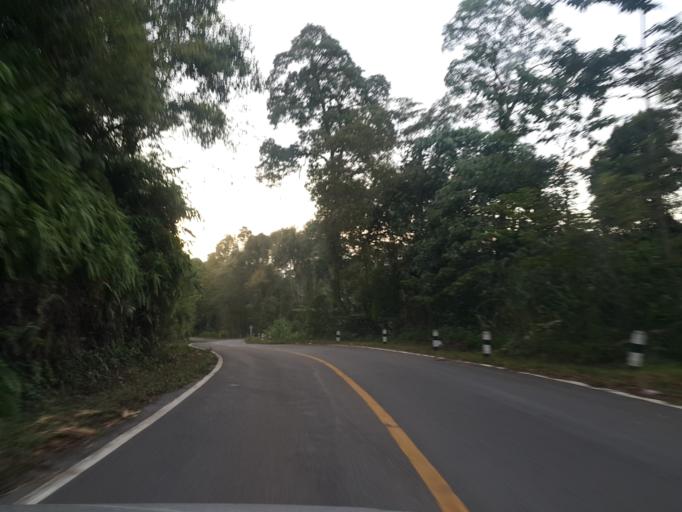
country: TH
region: Mae Hong Son
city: Khun Yuam
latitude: 18.7988
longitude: 98.0808
